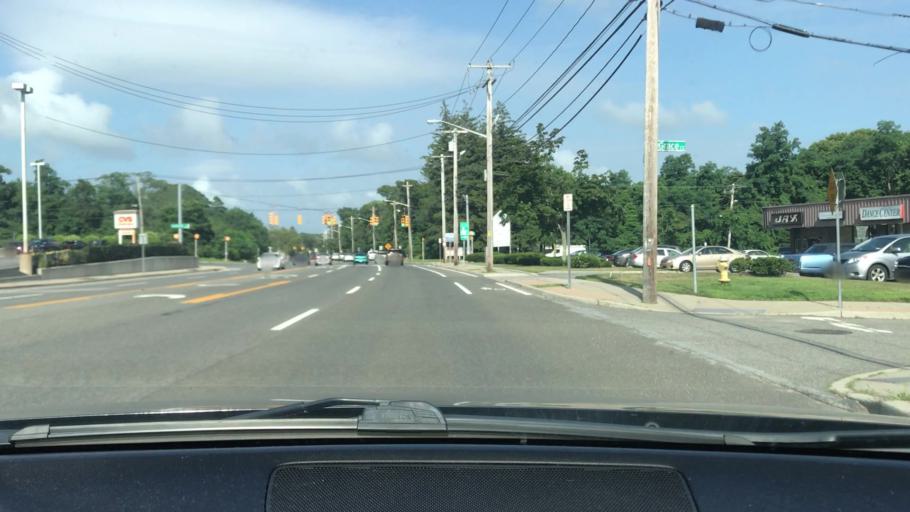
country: US
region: New York
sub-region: Suffolk County
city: Holbrook
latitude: 40.8320
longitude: -73.0830
